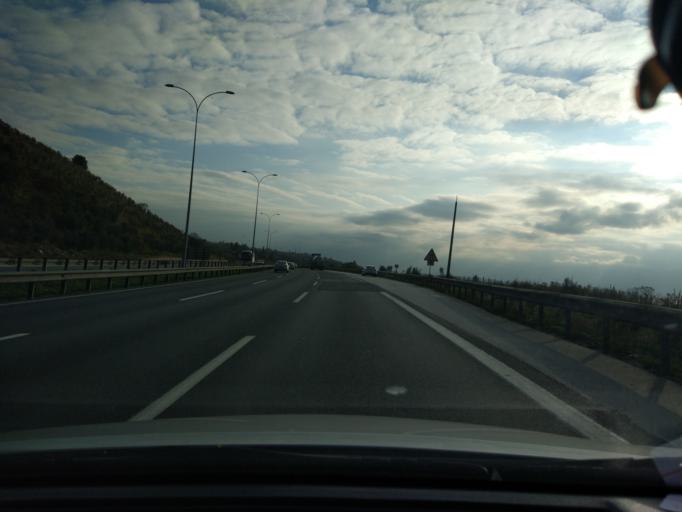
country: TR
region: Kocaeli
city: Tavsancil
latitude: 40.7737
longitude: 29.5517
